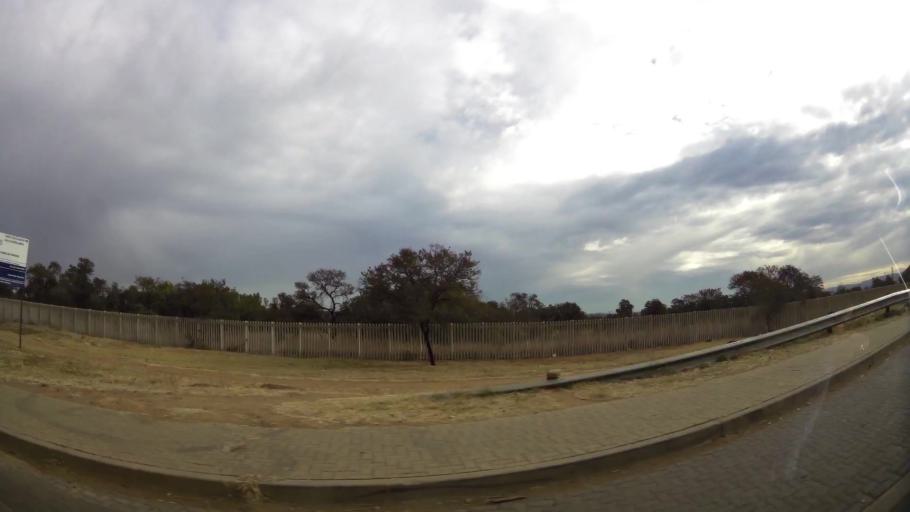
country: ZA
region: Gauteng
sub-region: City of Tshwane Metropolitan Municipality
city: Pretoria
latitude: -25.7211
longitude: 28.3094
